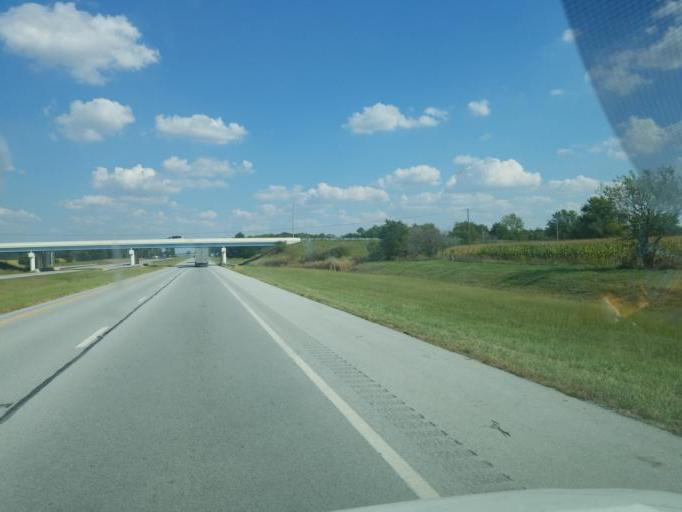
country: US
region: Ohio
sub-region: Allen County
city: Lima
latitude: 40.8242
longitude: -84.0727
